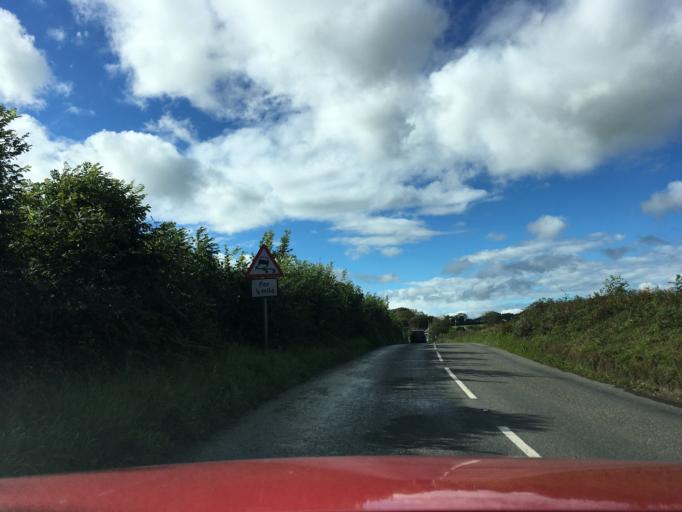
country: GB
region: England
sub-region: Devon
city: Totnes
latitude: 50.3613
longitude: -3.6750
